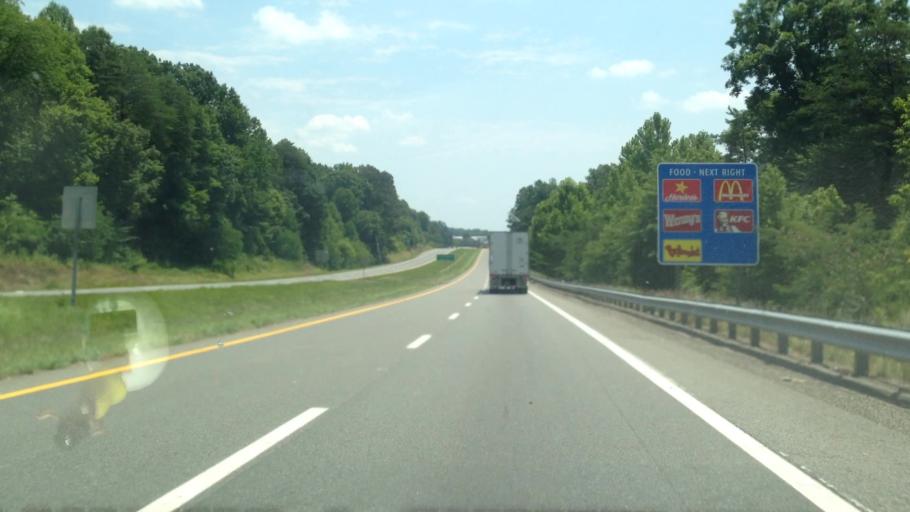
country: US
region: Virginia
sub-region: City of Martinsville
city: Martinsville
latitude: 36.6253
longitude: -79.8730
